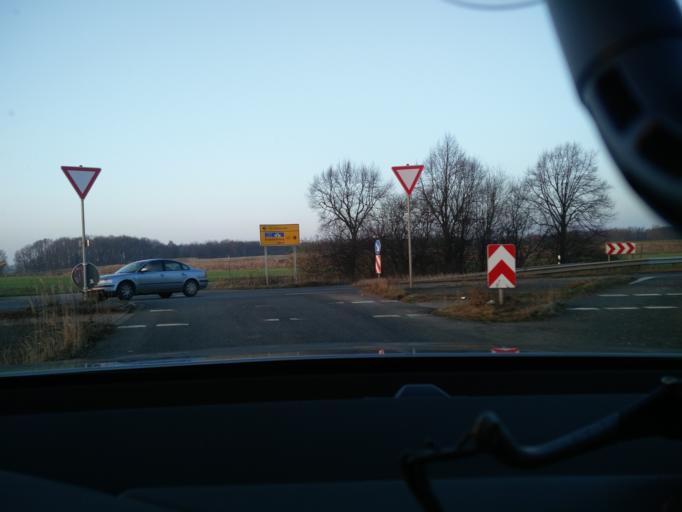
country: DE
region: Lower Saxony
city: Peine
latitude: 52.3038
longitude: 10.2054
